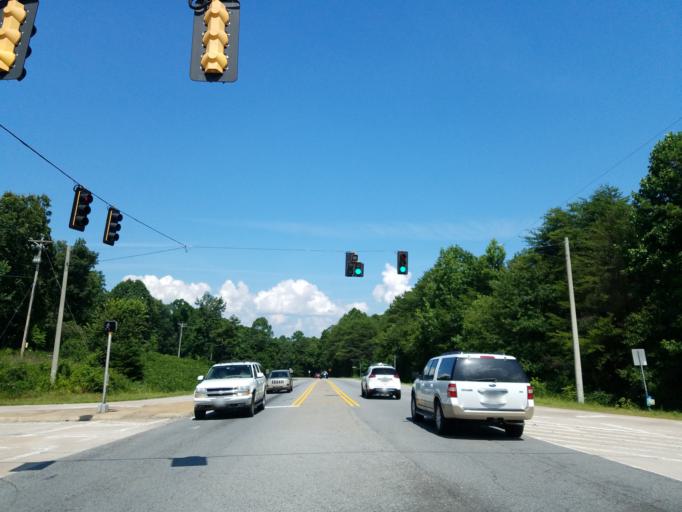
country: US
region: Georgia
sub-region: Forsyth County
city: Cumming
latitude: 34.2293
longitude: -84.1004
